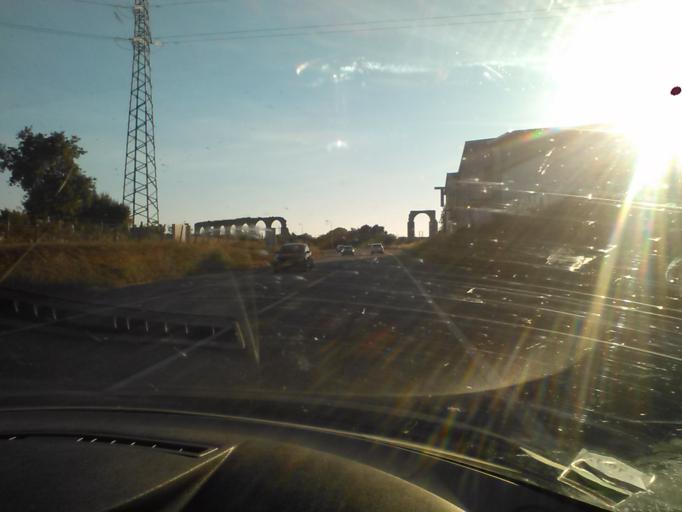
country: PT
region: Porto
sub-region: Vila do Conde
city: Vila do Conde
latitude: 41.3684
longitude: -8.7379
